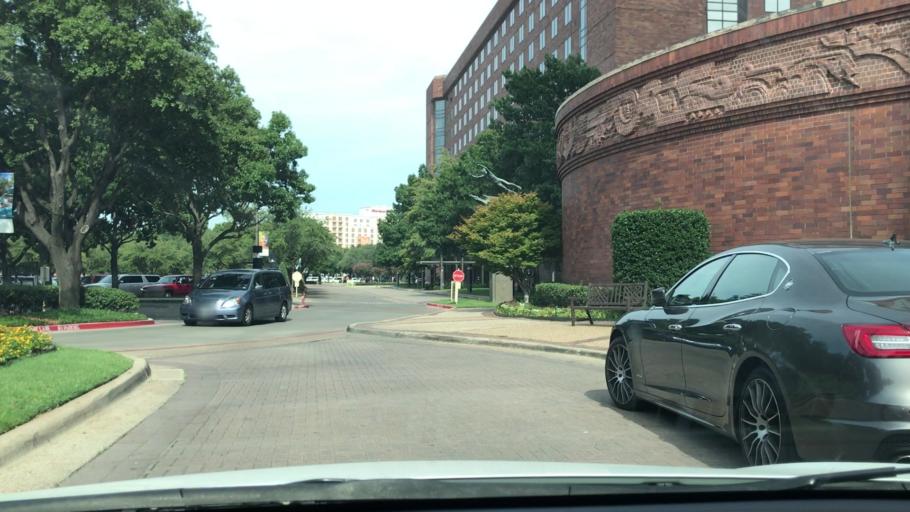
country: US
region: Texas
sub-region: Dallas County
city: Dallas
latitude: 32.8006
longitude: -96.8299
